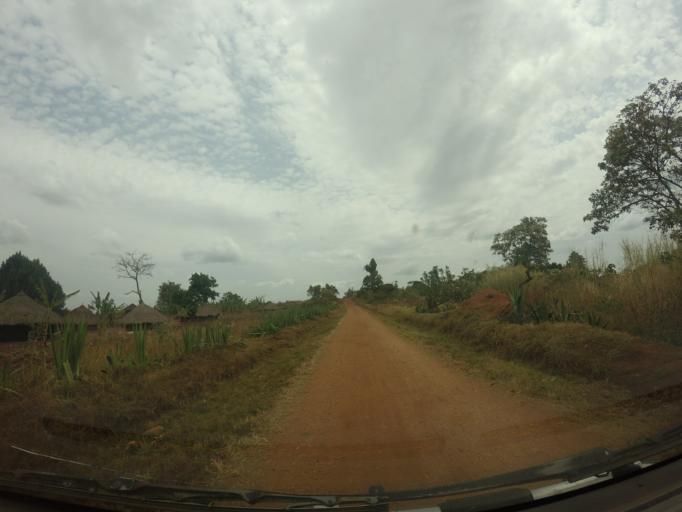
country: UG
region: Northern Region
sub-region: Arua District
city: Arua
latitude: 2.8232
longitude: 30.9042
